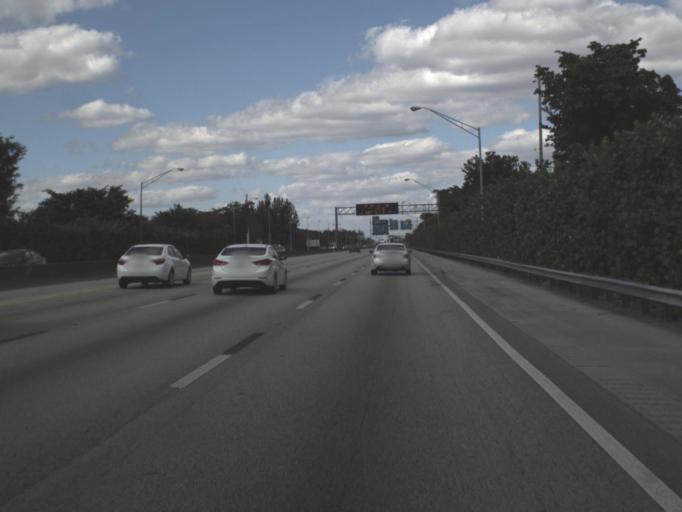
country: US
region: Florida
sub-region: Broward County
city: Davie
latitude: 26.0483
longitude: -80.2147
